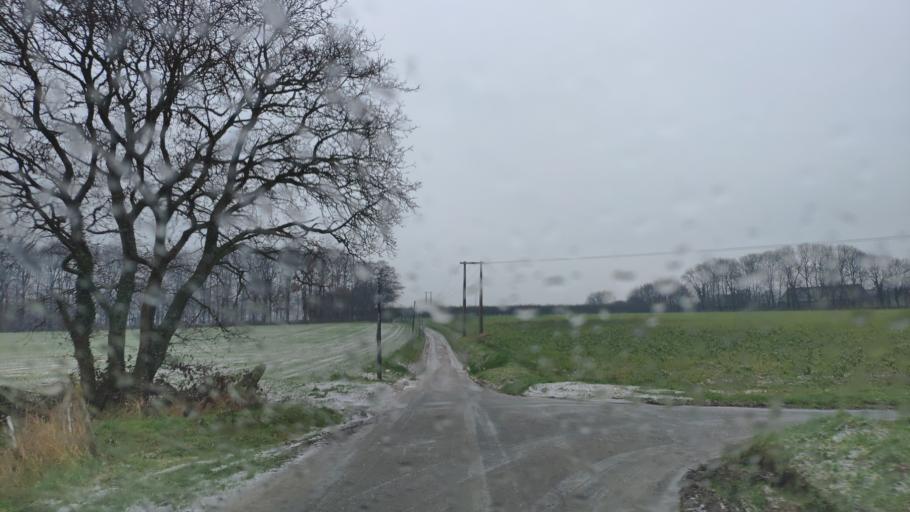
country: FR
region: Haute-Normandie
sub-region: Departement de la Seine-Maritime
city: Neville
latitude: 49.7936
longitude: 0.6955
